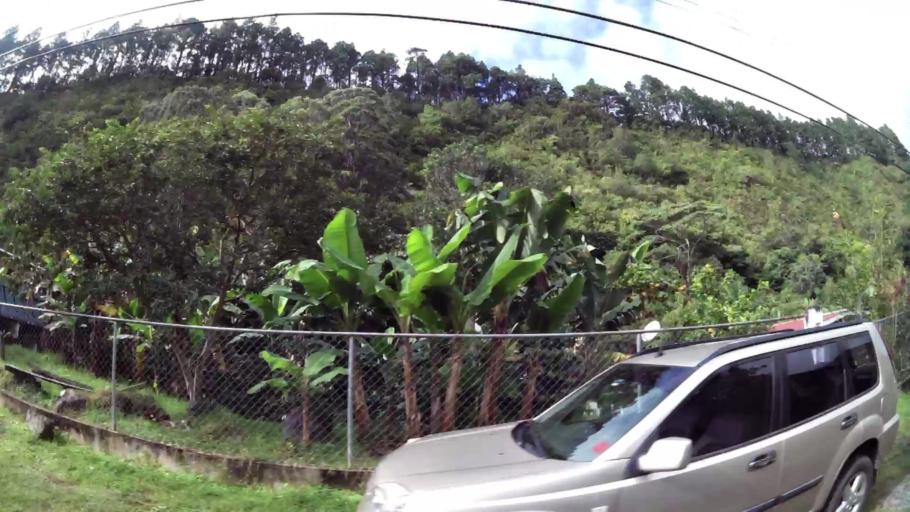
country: PA
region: Chiriqui
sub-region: Distrito Boquete
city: Boquete
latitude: 8.7894
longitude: -82.4413
